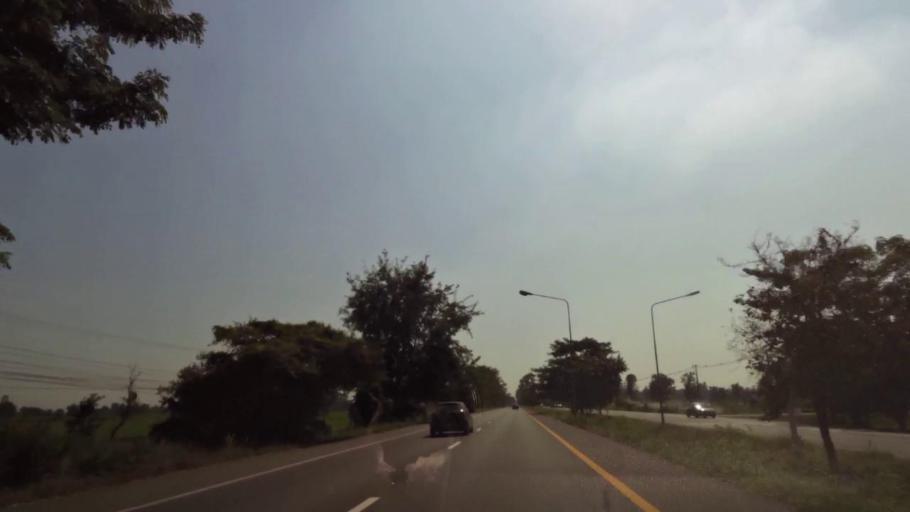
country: TH
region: Nakhon Sawan
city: Banphot Phisai
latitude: 16.0084
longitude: 100.1154
